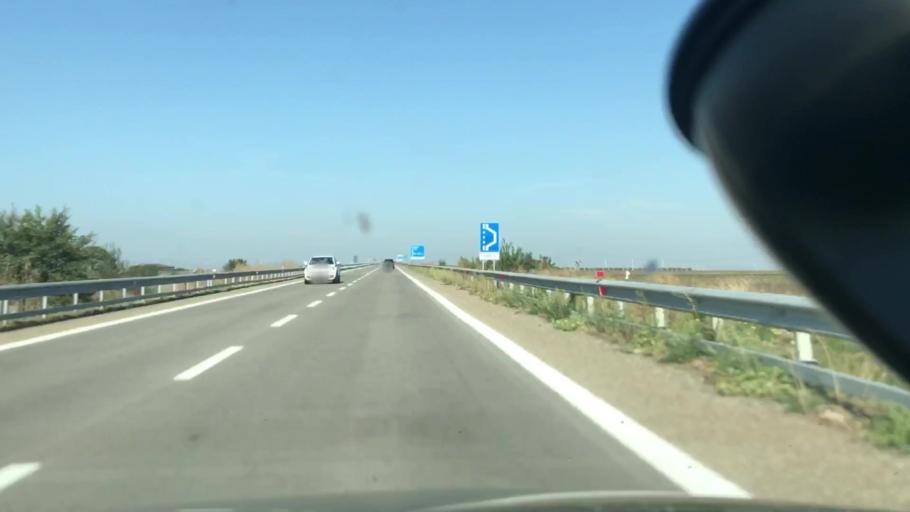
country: IT
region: Basilicate
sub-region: Provincia di Potenza
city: Montemilone
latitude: 40.9909
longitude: 15.8981
